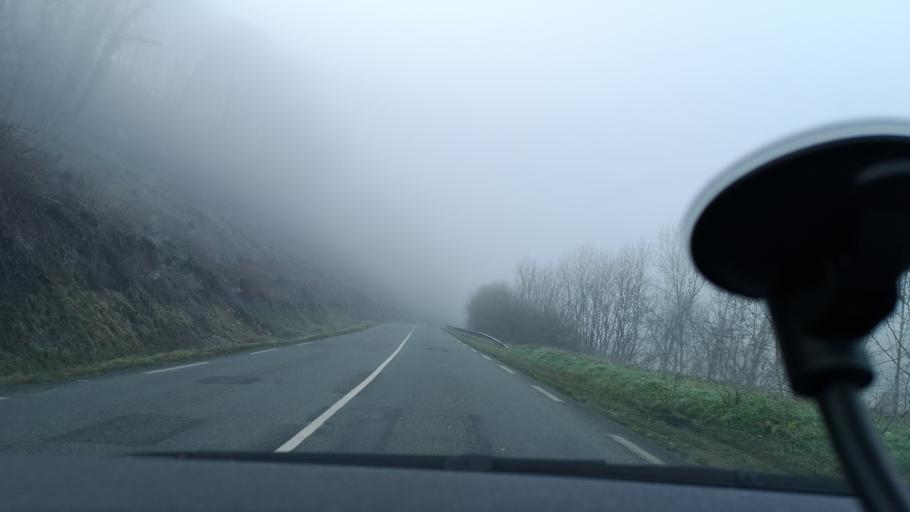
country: FR
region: Franche-Comte
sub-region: Departement du Doubs
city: Clerval
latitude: 47.4127
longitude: 6.5504
